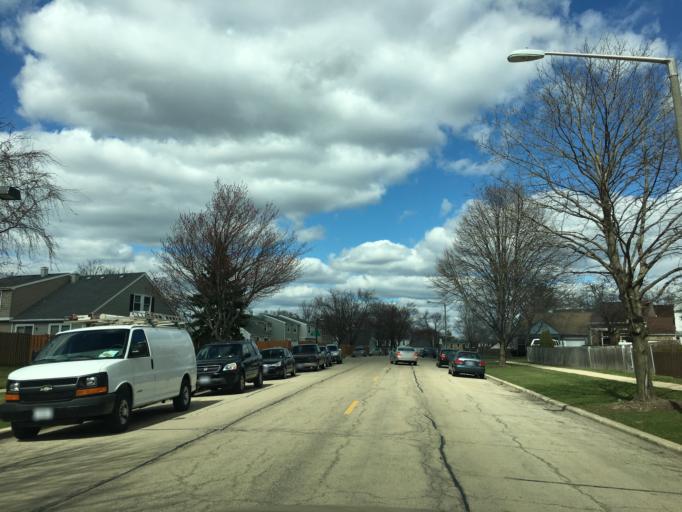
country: US
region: Illinois
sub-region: DuPage County
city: Hanover Park
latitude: 42.0068
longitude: -88.1301
